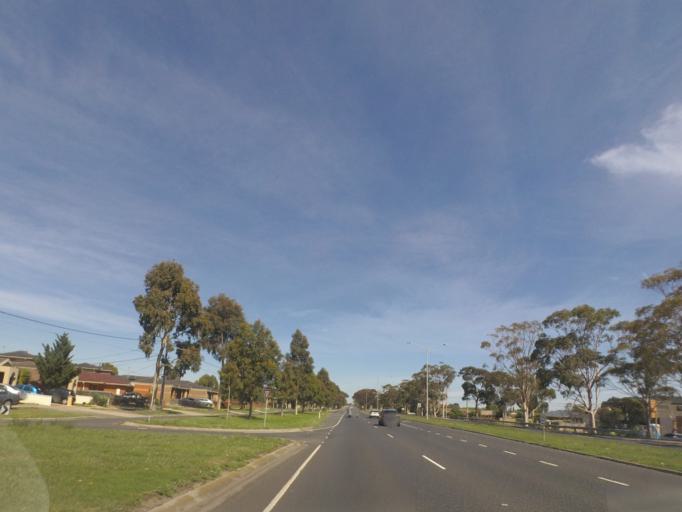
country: AU
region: Victoria
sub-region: Brimbank
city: Deer Park
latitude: -37.7668
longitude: 144.7641
